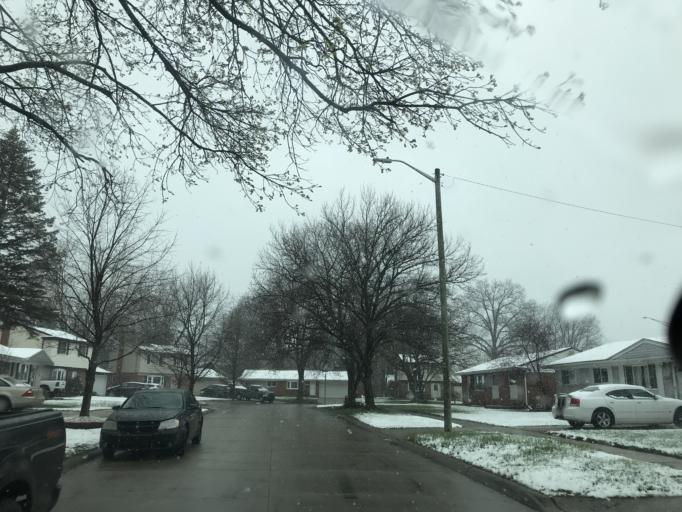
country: US
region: Michigan
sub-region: Wayne County
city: Taylor
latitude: 42.2304
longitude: -83.2522
